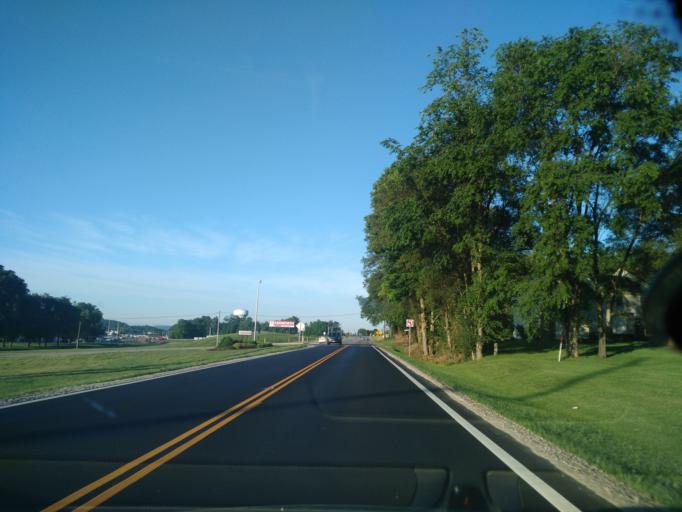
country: US
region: Ohio
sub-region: Ross County
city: Chillicothe
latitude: 39.4003
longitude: -82.9624
